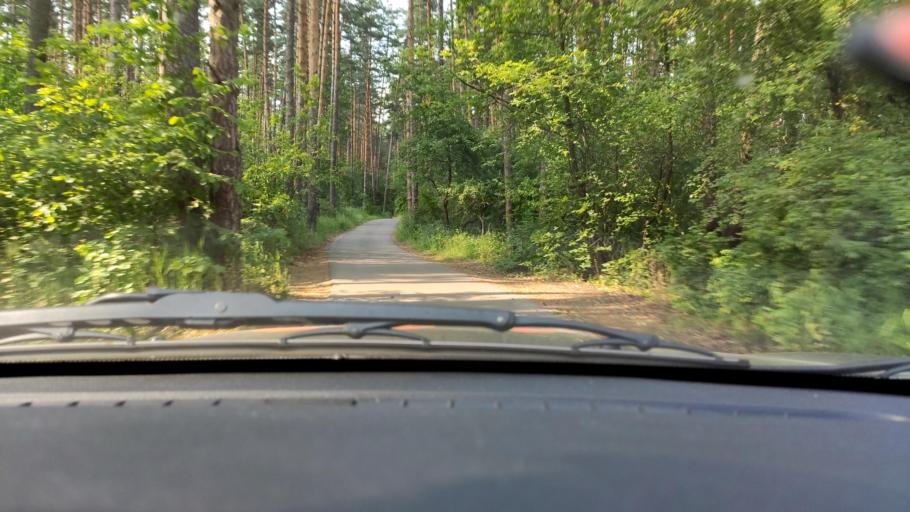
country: RU
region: Voronezj
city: Somovo
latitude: 51.7946
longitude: 39.3810
